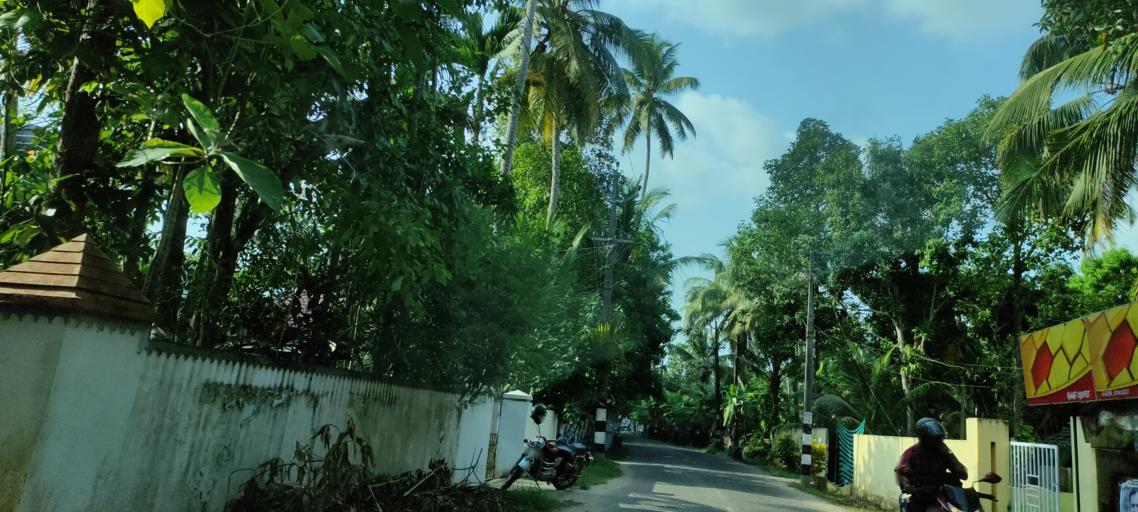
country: IN
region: Kerala
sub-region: Alappuzha
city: Vayalar
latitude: 9.7014
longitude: 76.2896
